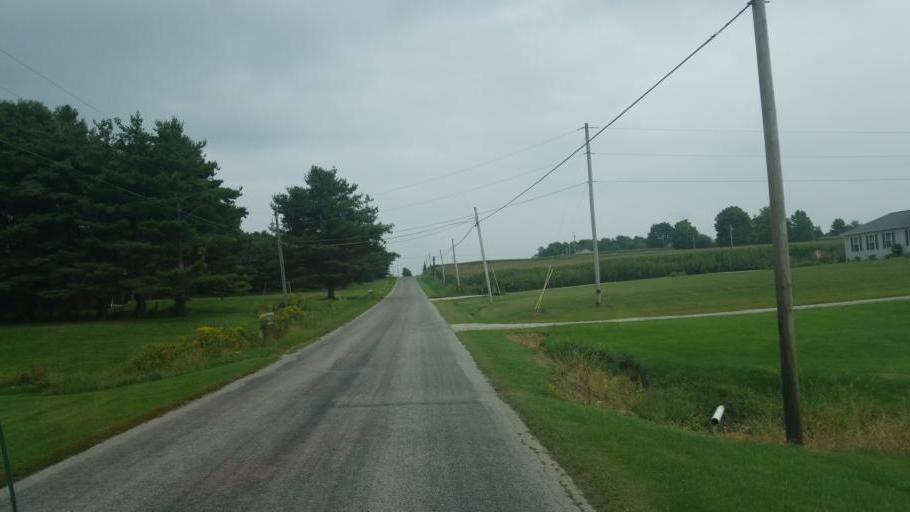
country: US
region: Ohio
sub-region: Wayne County
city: Creston
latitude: 40.9597
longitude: -81.9262
